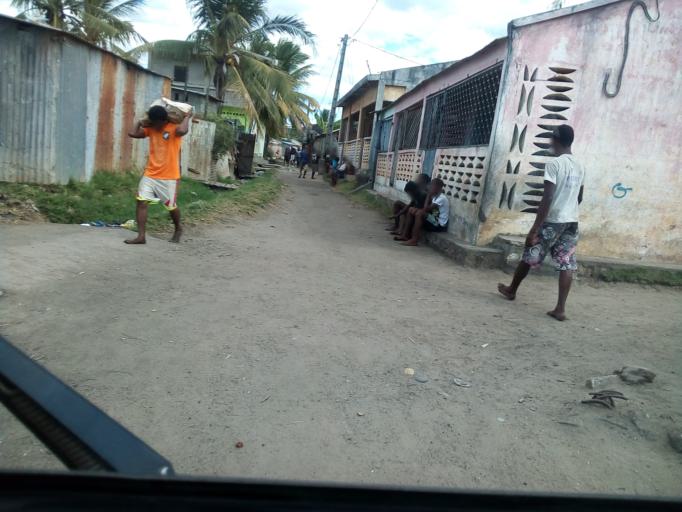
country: MG
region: Boeny
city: Mahajanga
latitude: -15.7170
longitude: 46.3281
